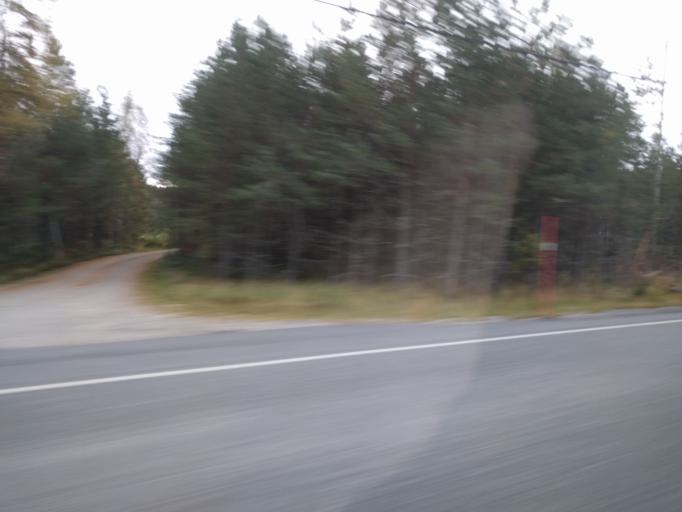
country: NO
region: Aust-Agder
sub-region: Evje og Hornnes
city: Evje
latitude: 58.4988
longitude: 7.7751
